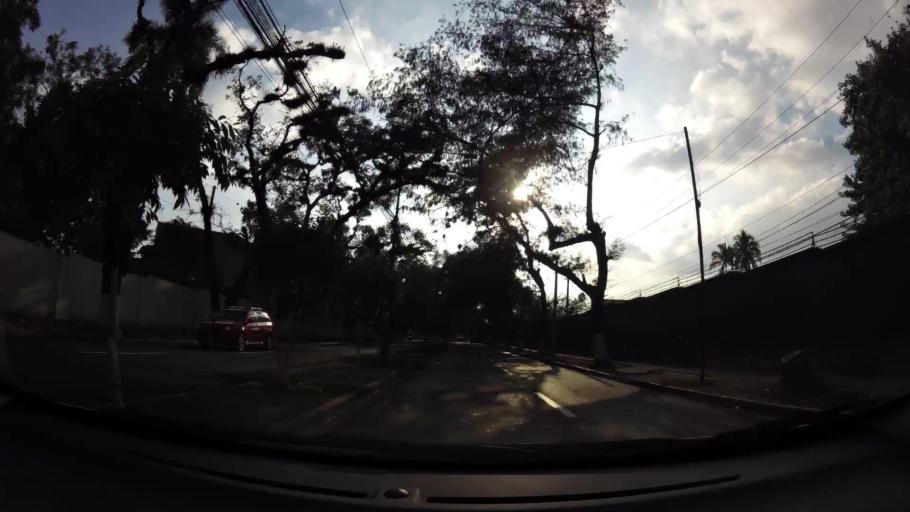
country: SV
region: La Libertad
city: Antiguo Cuscatlan
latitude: 13.6889
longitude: -89.2336
